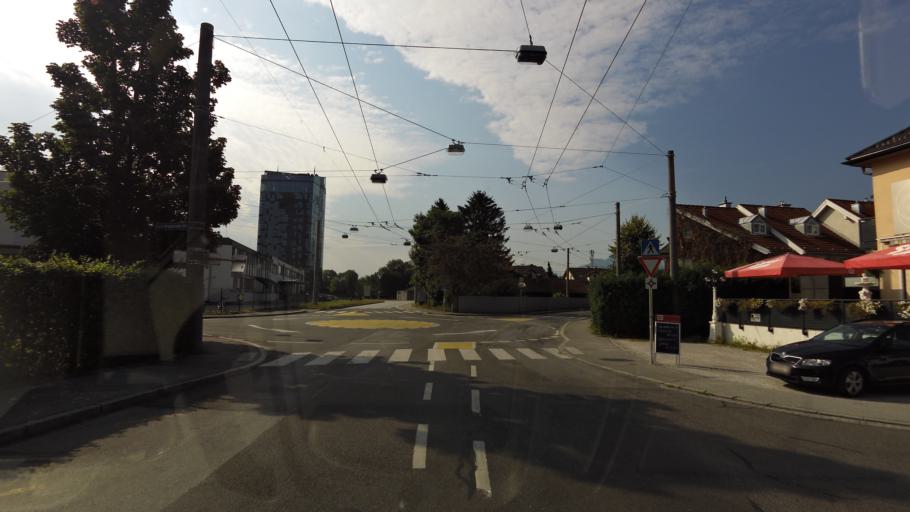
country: AT
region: Salzburg
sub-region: Politischer Bezirk Salzburg-Umgebung
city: Bergheim
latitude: 47.8291
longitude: 13.0227
